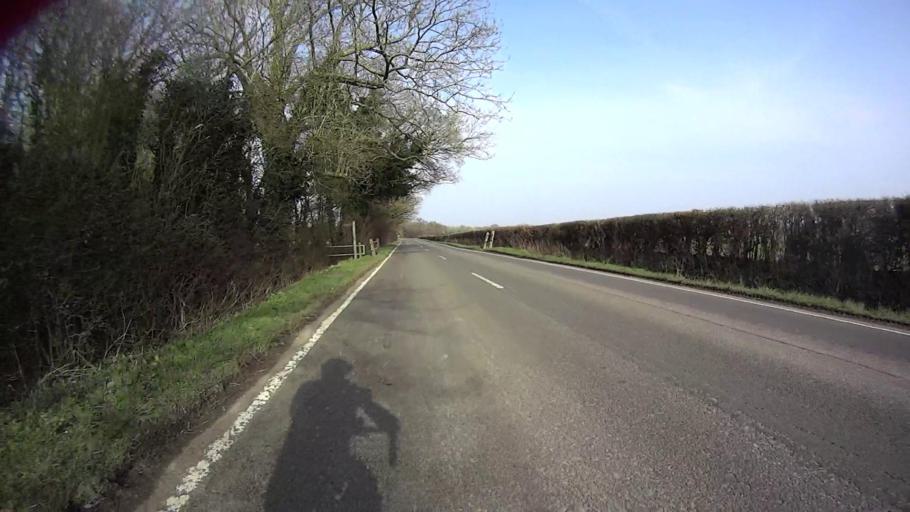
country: GB
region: England
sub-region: West Sussex
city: Copthorne
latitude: 51.1758
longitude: -0.0929
